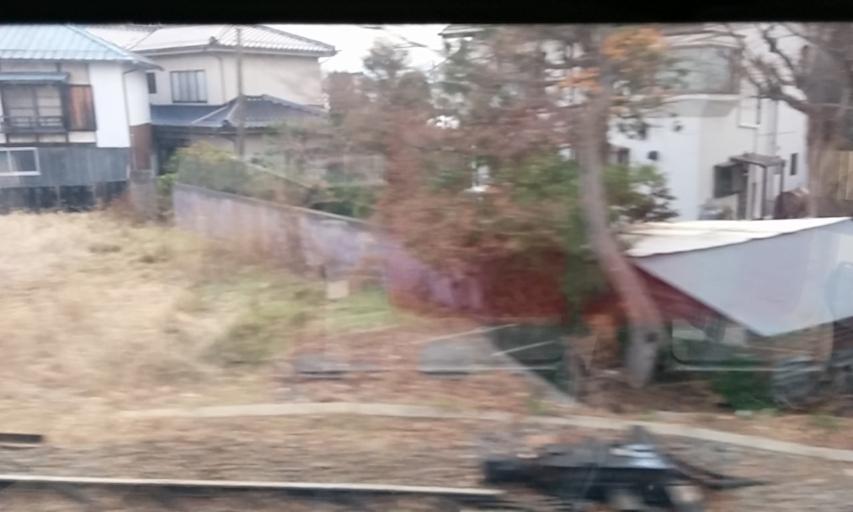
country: JP
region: Nagano
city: Matsumoto
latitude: 36.2383
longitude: 137.9600
